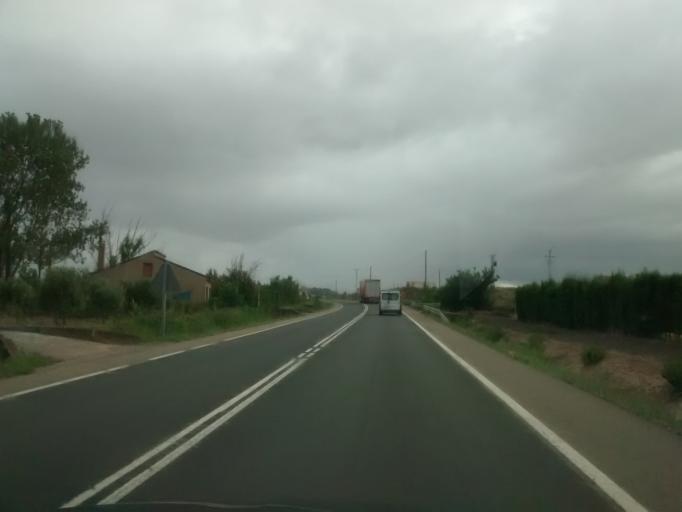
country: ES
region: Navarre
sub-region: Provincia de Navarra
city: Murchante
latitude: 42.0125
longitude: -1.6589
